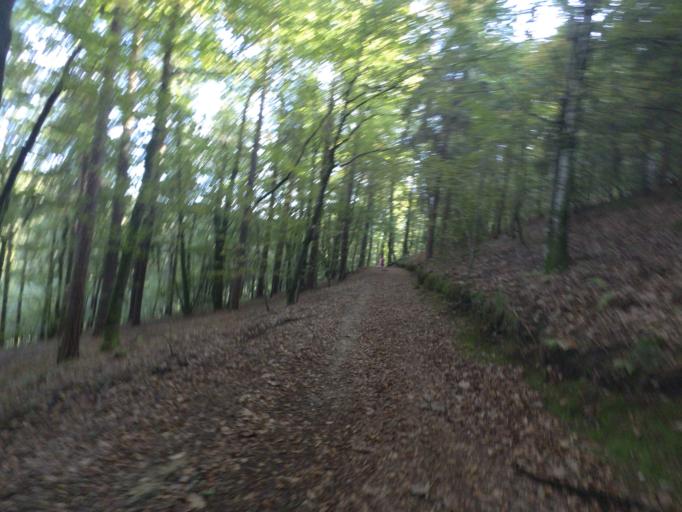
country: AT
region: Styria
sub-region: Politischer Bezirk Leibnitz
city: Kitzeck im Sausal
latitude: 46.7701
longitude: 15.4408
